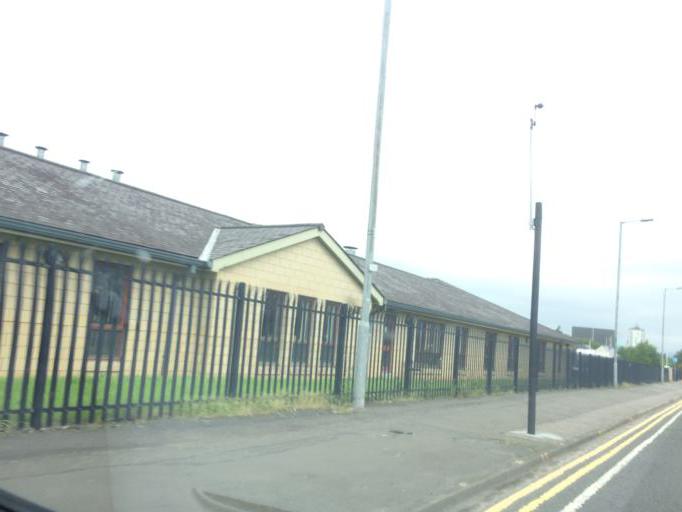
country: GB
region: Scotland
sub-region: East Dunbartonshire
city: Bearsden
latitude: 55.8631
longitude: -4.3356
